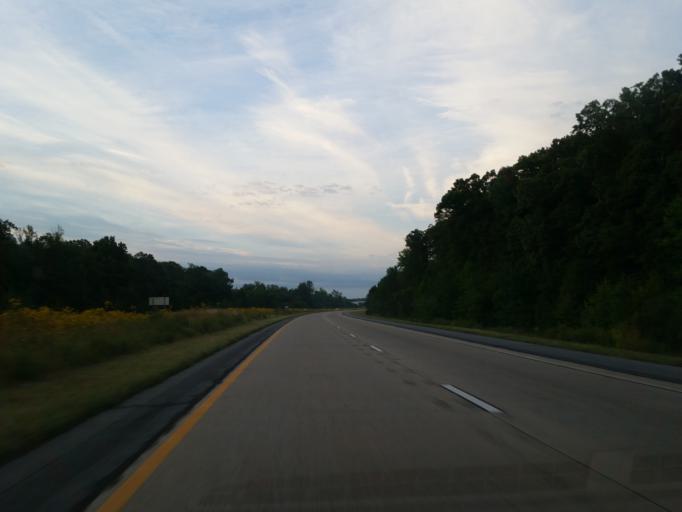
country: US
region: Delaware
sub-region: Kent County
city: Cheswold
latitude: 39.2620
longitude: -75.5788
